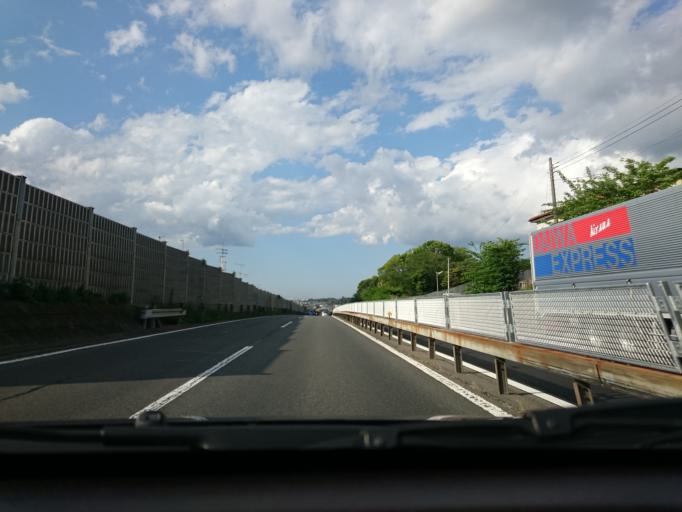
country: JP
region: Kanagawa
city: Isehara
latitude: 35.3530
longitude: 139.2992
